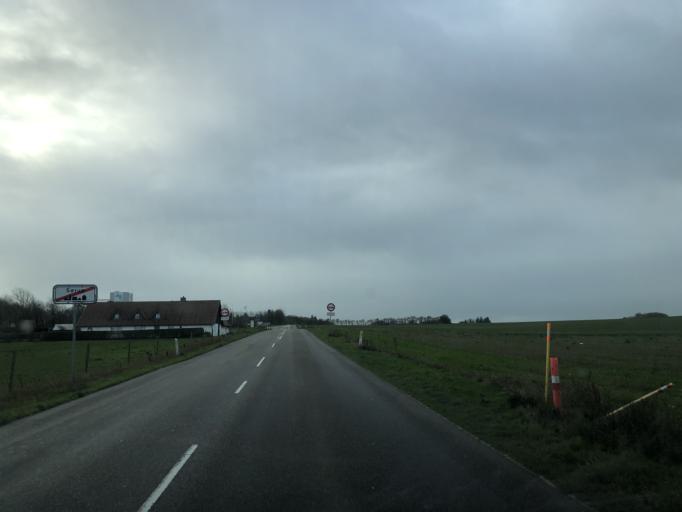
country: DK
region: North Denmark
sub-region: Rebild Kommune
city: Stovring
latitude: 56.8858
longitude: 9.7841
